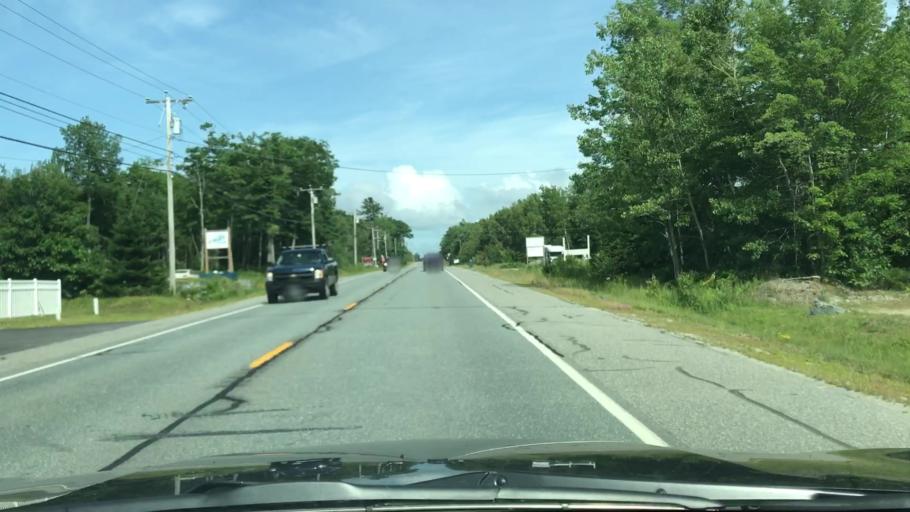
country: US
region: Maine
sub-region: Hancock County
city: Ellsworth
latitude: 44.5394
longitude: -68.4535
